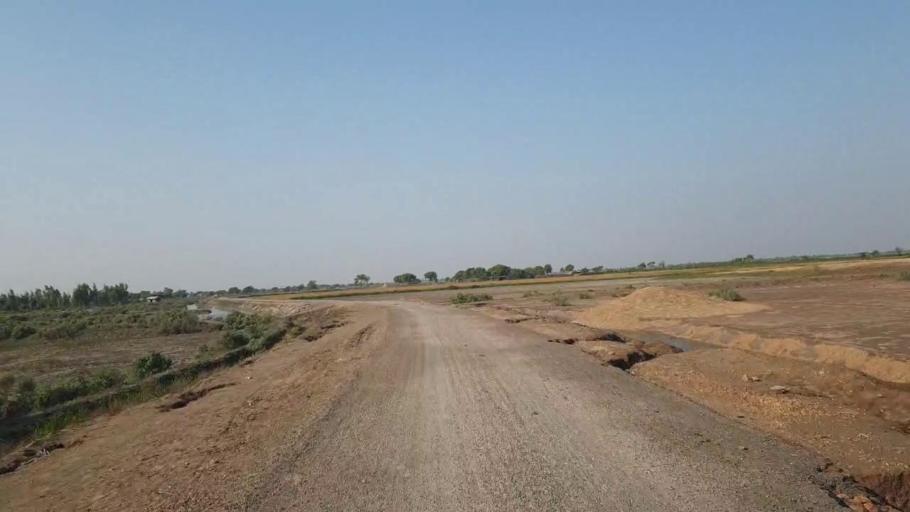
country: PK
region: Sindh
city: Kario
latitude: 24.8995
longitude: 68.6226
